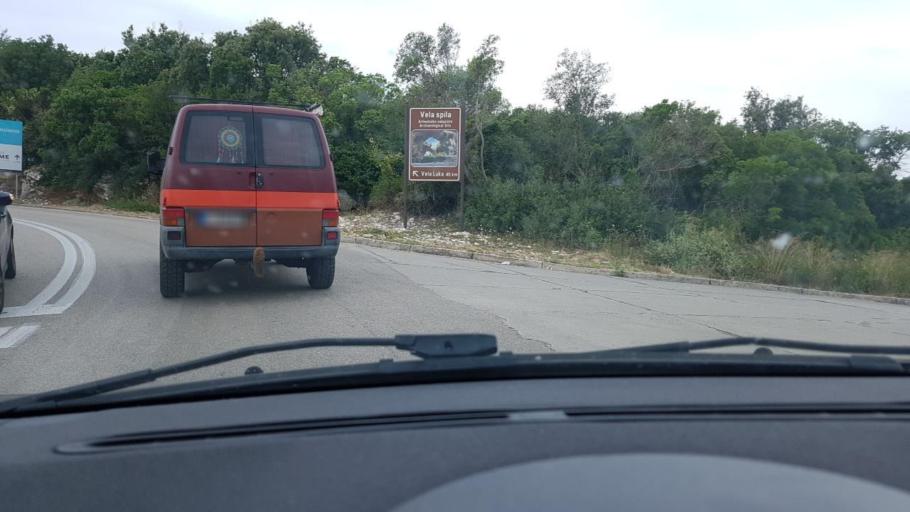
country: HR
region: Dubrovacko-Neretvanska
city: Korcula
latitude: 42.9537
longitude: 17.1492
